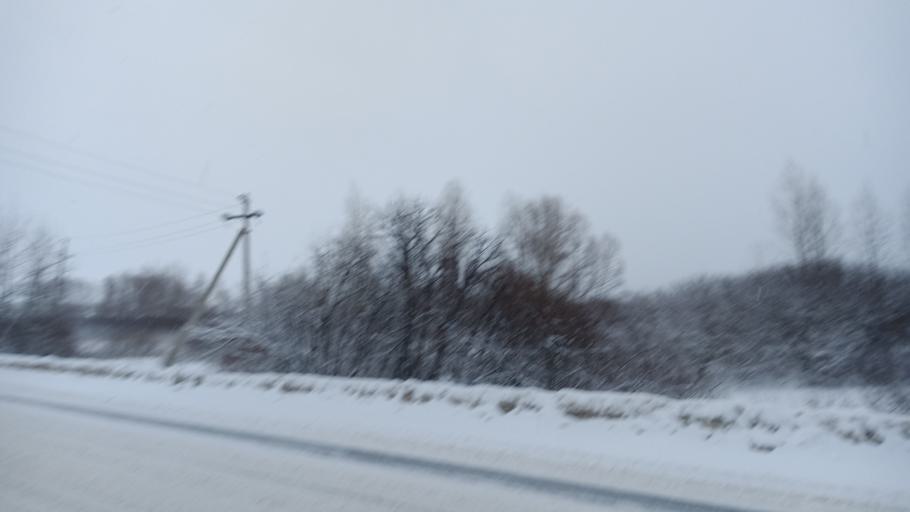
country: RU
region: Altai Krai
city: Zaton
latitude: 53.3121
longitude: 83.8309
